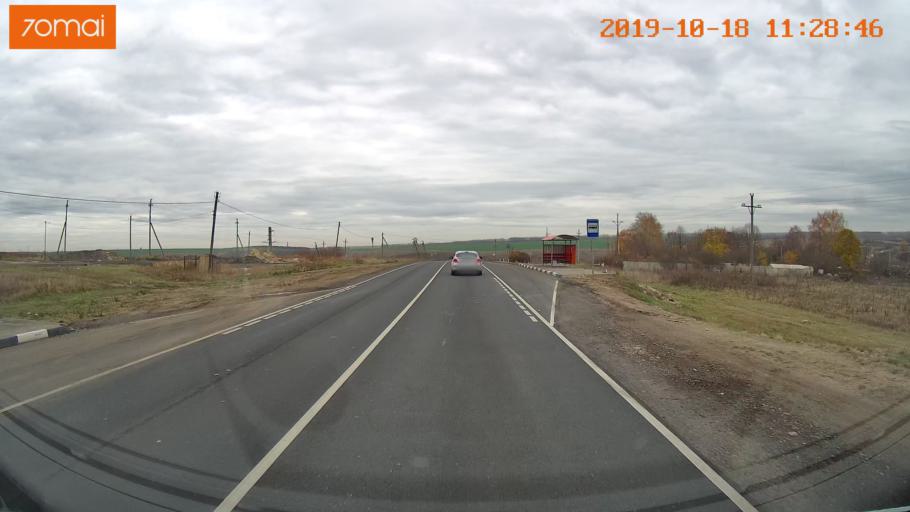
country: RU
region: Tula
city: Kimovsk
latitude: 54.1558
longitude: 38.6662
